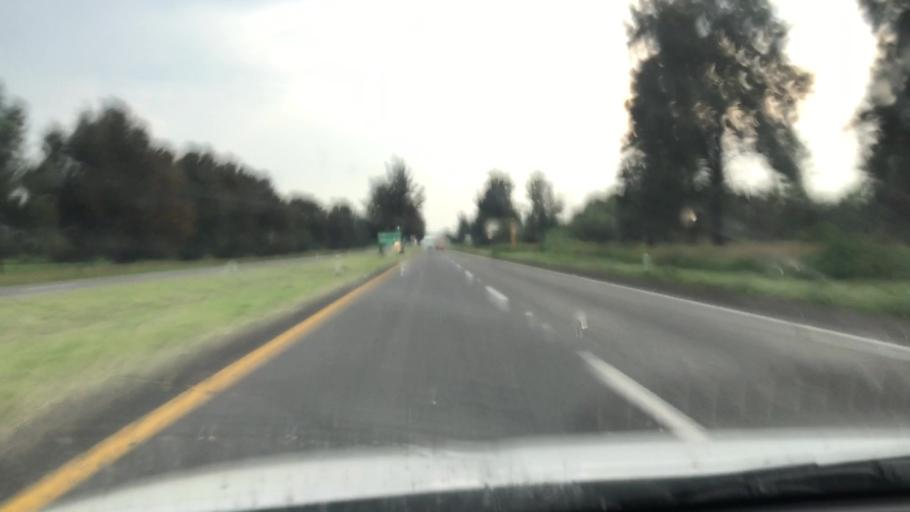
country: MX
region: Michoacan
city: Vistahermosa de Negrete
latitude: 20.2825
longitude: -102.4584
